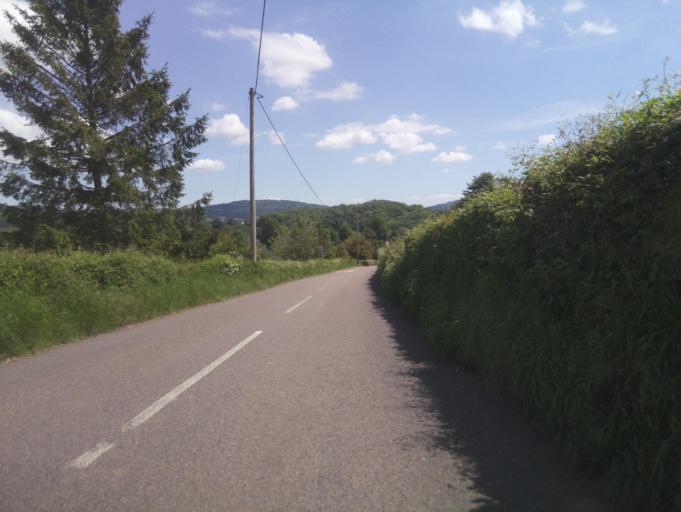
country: GB
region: England
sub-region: Herefordshire
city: Llanrothal
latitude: 51.8338
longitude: -2.7573
